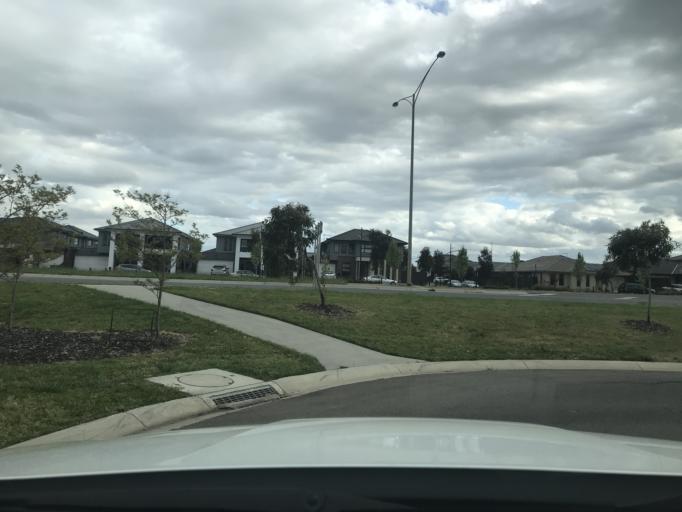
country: AU
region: Victoria
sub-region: Hume
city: Roxburgh Park
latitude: -37.5912
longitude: 144.8933
